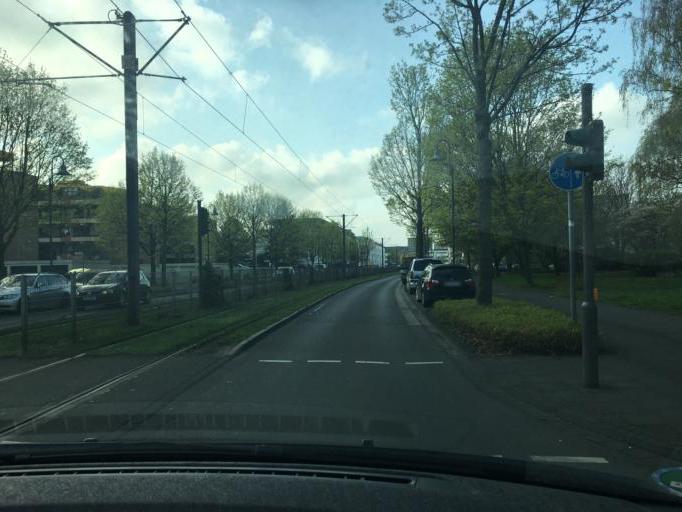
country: DE
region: North Rhine-Westphalia
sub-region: Regierungsbezirk Koln
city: Bonn
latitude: 50.7539
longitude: 7.0791
